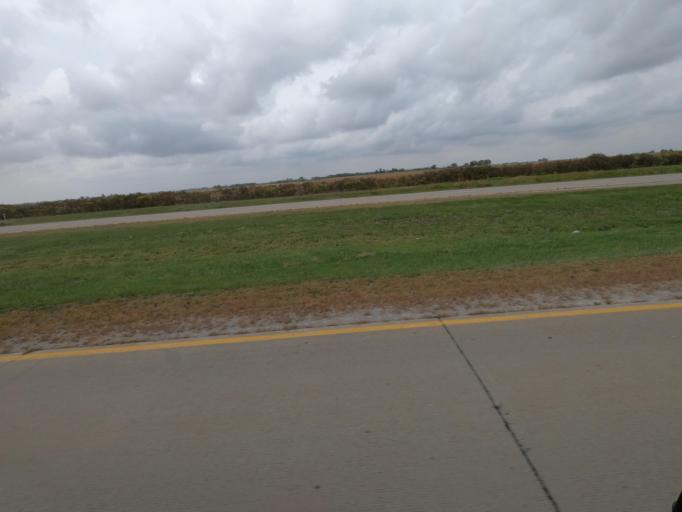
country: US
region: Iowa
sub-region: Wapello County
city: Ottumwa
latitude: 41.0019
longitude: -92.2522
